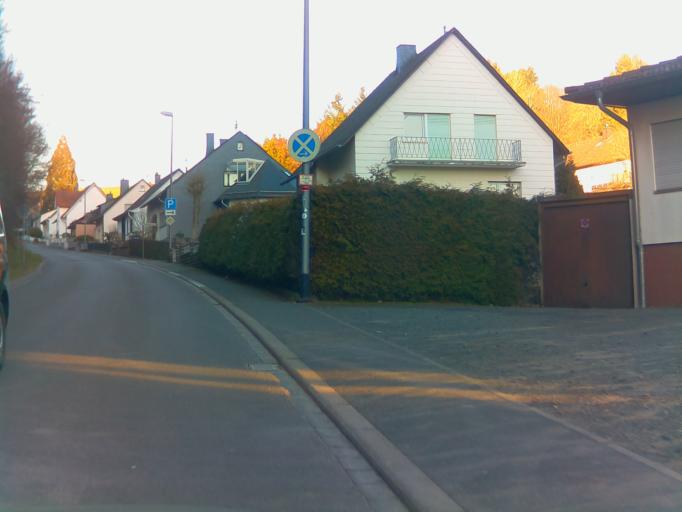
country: DE
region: Rheinland-Pfalz
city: Herrstein
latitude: 49.7821
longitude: 7.3396
